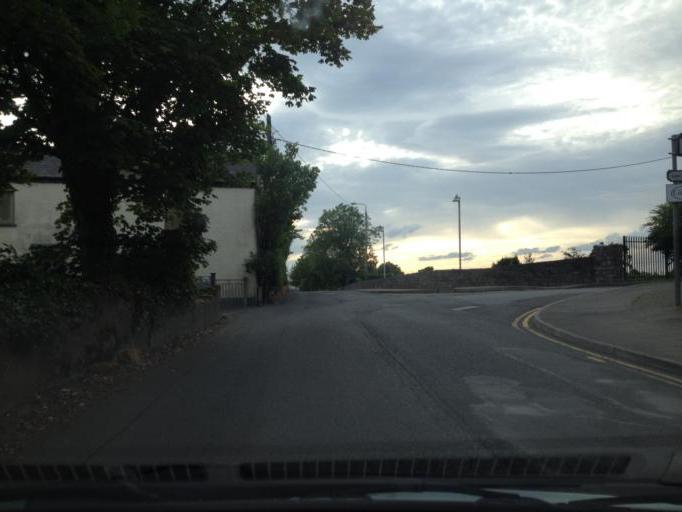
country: IE
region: Connaught
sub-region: Sligo
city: Sligo
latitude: 54.2806
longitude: -8.4628
